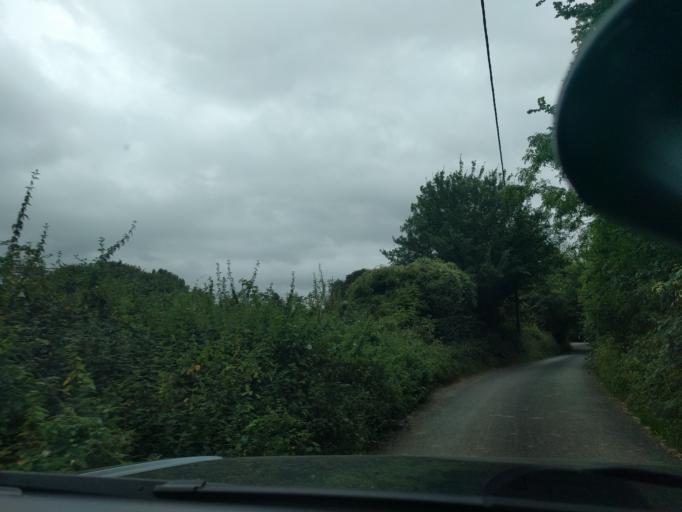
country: GB
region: England
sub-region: Wiltshire
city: Neston
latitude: 51.4124
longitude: -2.1805
